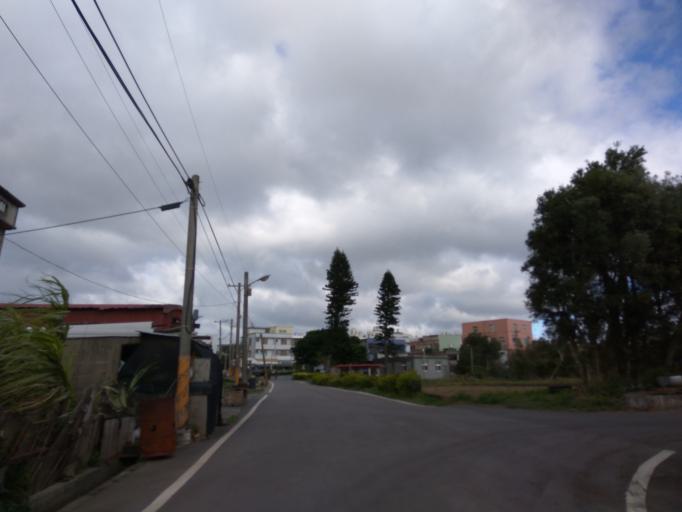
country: TW
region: Taiwan
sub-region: Hsinchu
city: Zhubei
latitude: 24.9731
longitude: 121.0811
